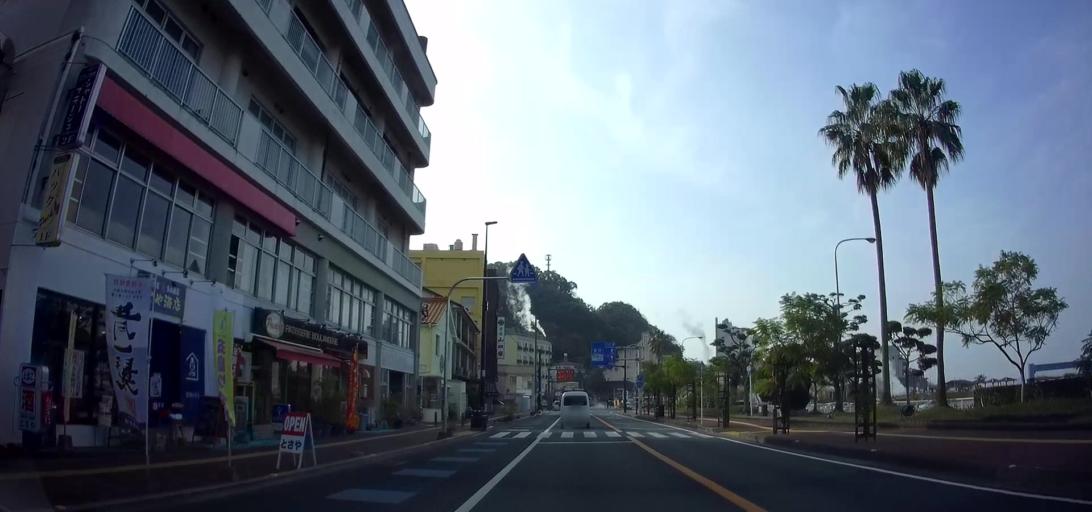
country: JP
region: Nagasaki
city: Shimabara
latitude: 32.7279
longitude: 130.2067
